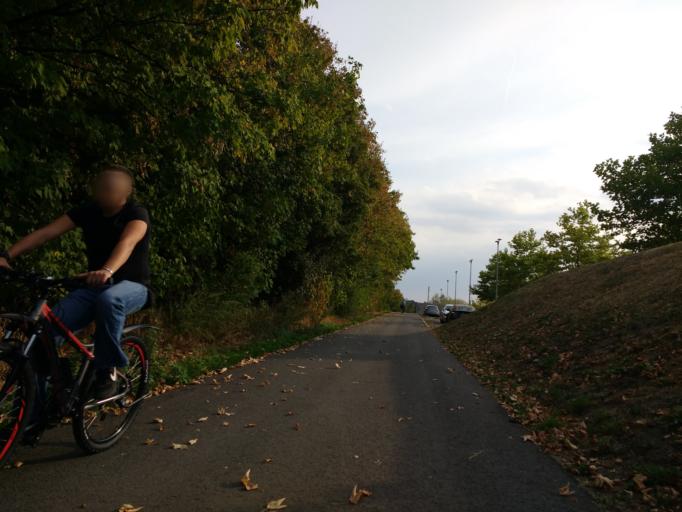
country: DE
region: Lower Saxony
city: Wolfsburg
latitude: 52.4204
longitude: 10.7470
